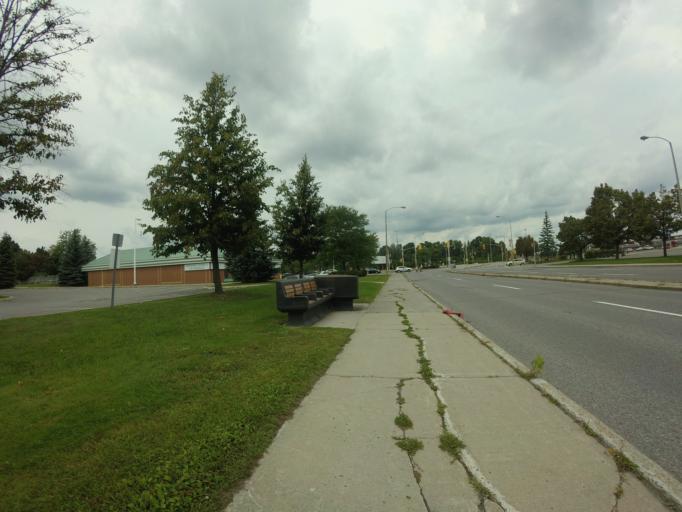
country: CA
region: Quebec
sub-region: Outaouais
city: Gatineau
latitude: 45.4766
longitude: -75.5197
